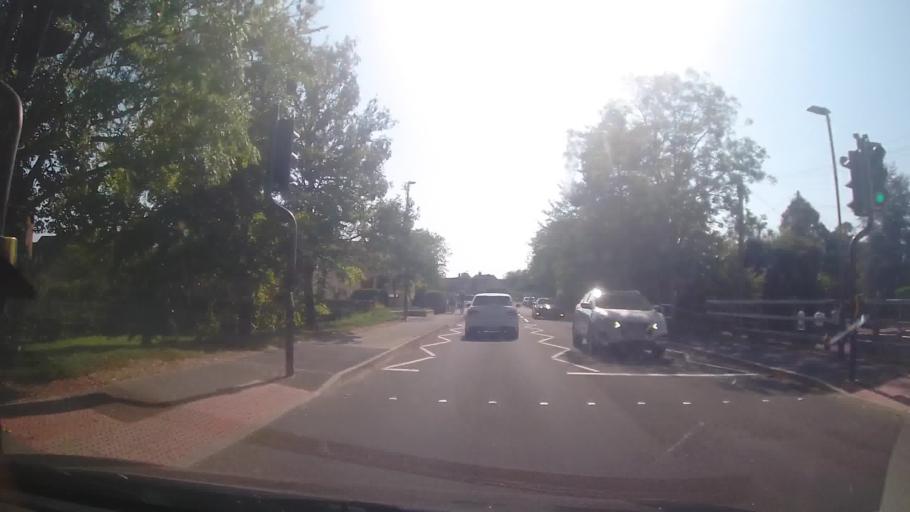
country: GB
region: England
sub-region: Gloucestershire
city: Bourton on the Water
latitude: 51.8896
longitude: -1.7571
